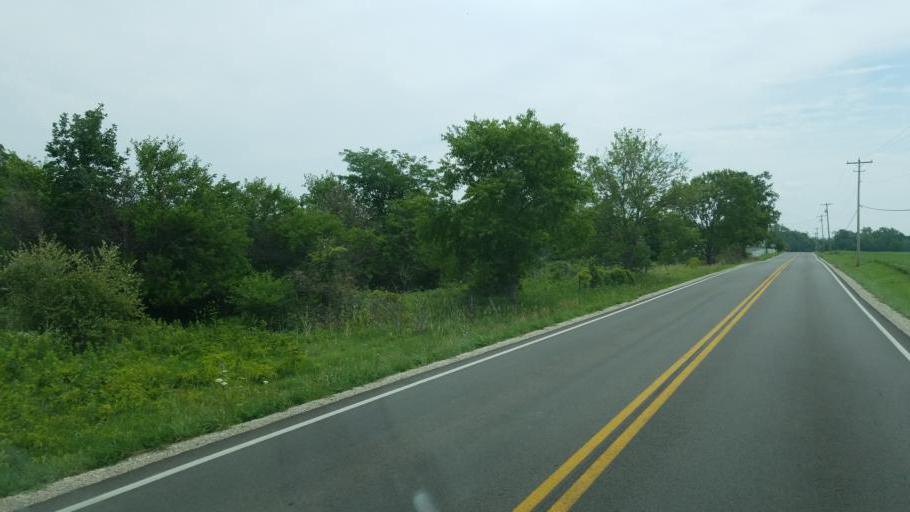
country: US
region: Ohio
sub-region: Madison County
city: Plain City
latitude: 40.0418
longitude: -83.2626
